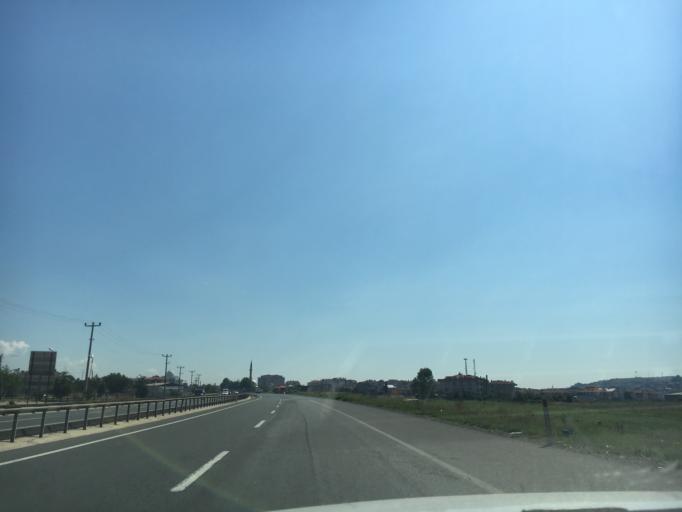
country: TR
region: Tekirdag
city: Marmara Ereglisi
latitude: 40.9726
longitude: 27.9405
